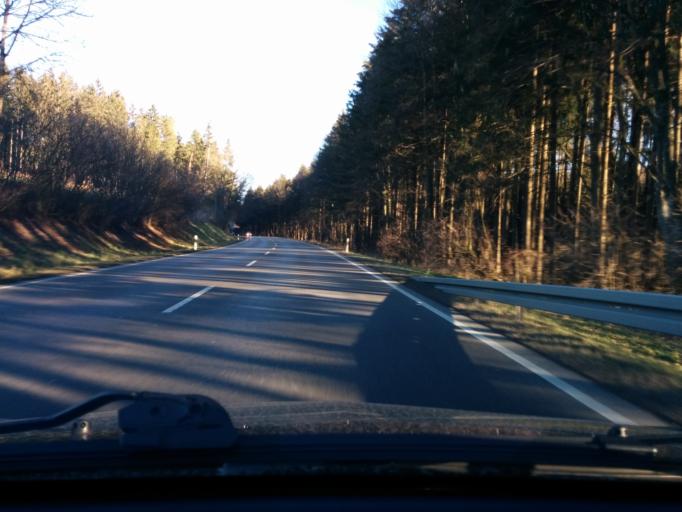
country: DE
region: Bavaria
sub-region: Upper Bavaria
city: Pahl
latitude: 47.9080
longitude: 11.2007
